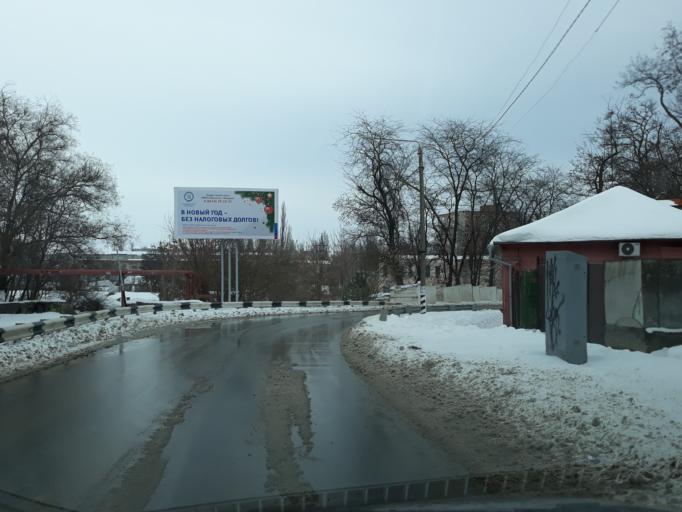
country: RU
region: Rostov
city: Taganrog
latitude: 47.2168
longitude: 38.9301
